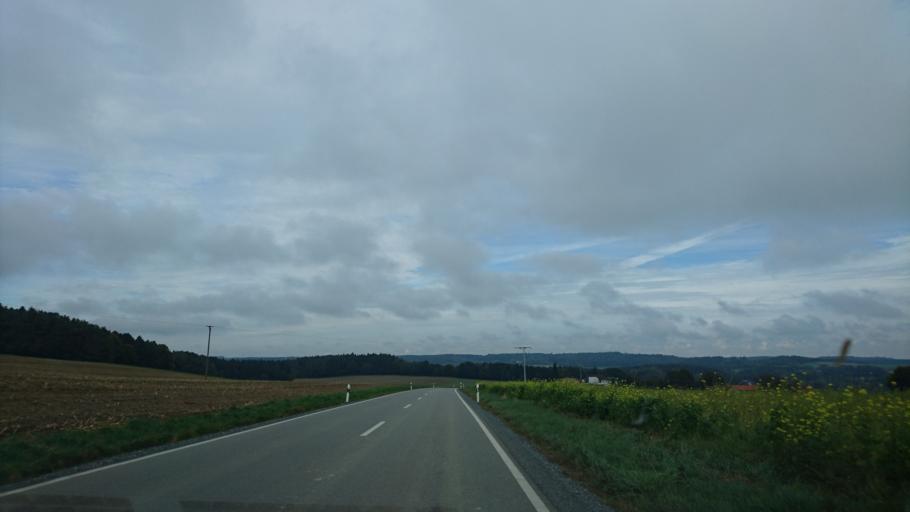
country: DE
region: Bavaria
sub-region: Upper Bavaria
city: Bruck
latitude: 48.0128
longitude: 11.8923
